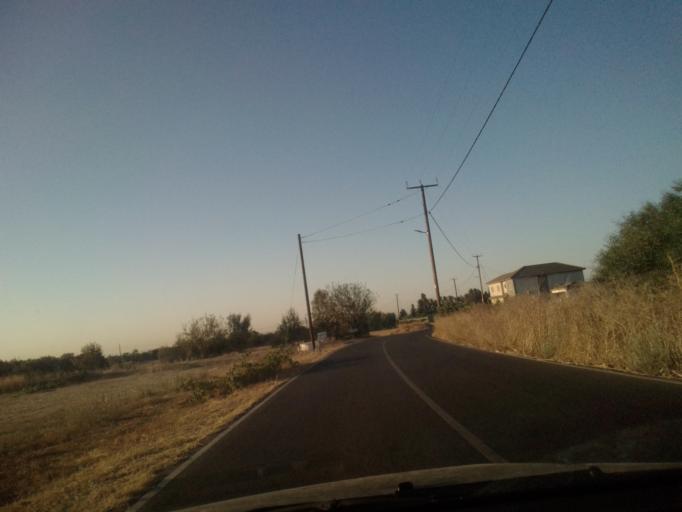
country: CY
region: Limassol
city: Ypsonas
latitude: 34.6730
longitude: 32.9589
